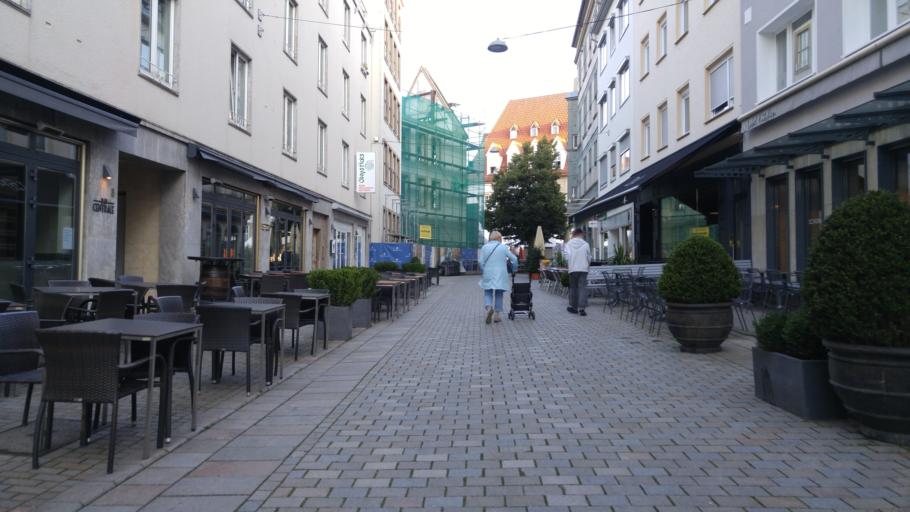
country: DE
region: North Rhine-Westphalia
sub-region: Regierungsbezirk Detmold
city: Bielefeld
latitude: 52.0198
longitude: 8.5325
